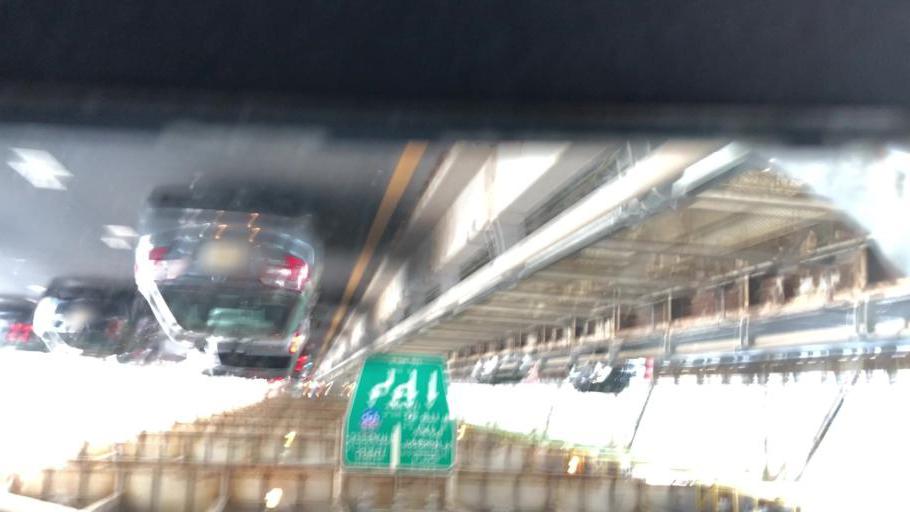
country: US
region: New Jersey
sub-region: Bergen County
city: Fort Lee
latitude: 40.8510
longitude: -73.9498
